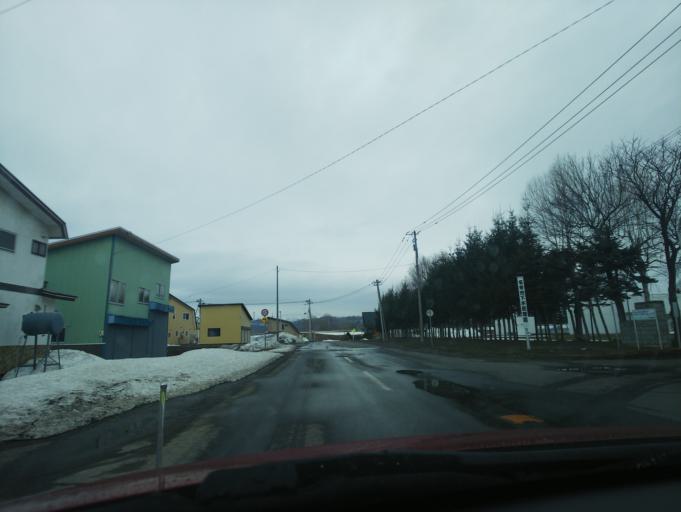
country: JP
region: Hokkaido
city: Nayoro
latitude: 44.3664
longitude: 142.4516
